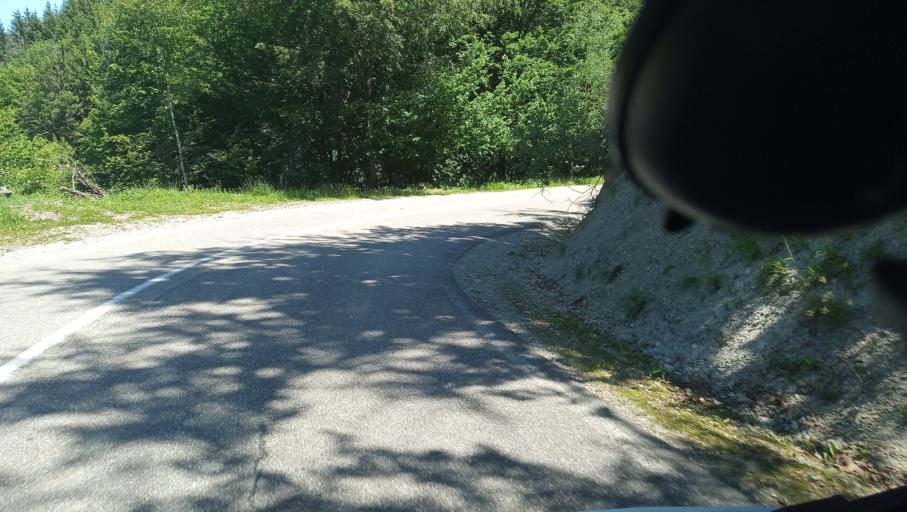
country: RO
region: Mehedinti
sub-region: Comuna Isverna
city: Isverna
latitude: 45.0462
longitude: 22.6211
